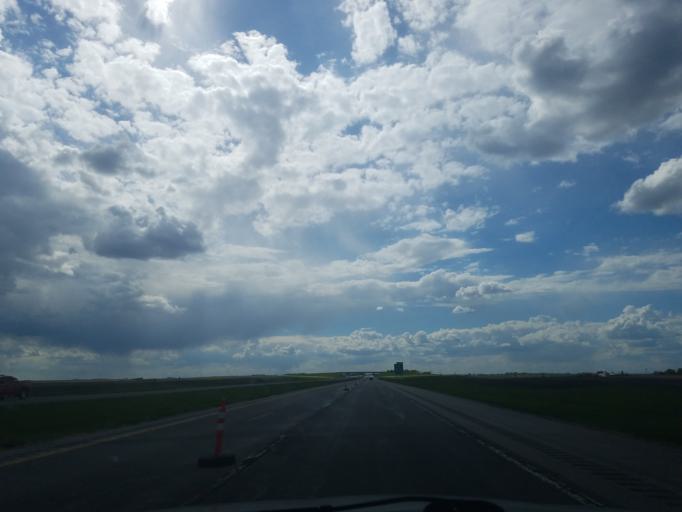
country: US
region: North Dakota
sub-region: Barnes County
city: Valley City
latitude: 46.9201
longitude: -97.7755
